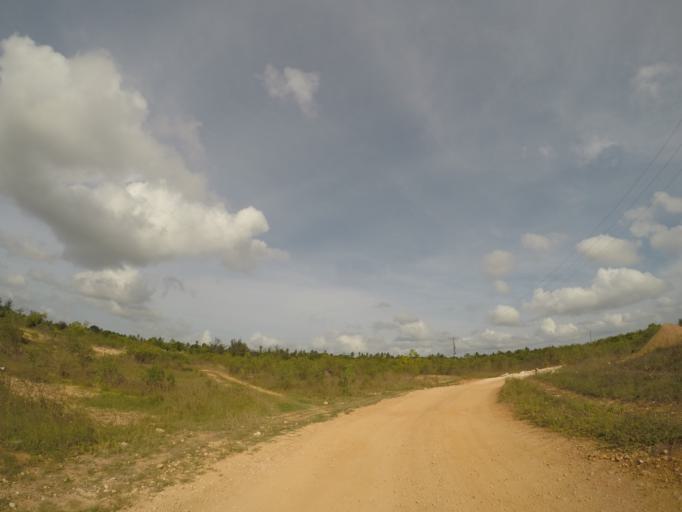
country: TZ
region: Zanzibar Central/South
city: Koani
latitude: -6.2306
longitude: 39.3205
